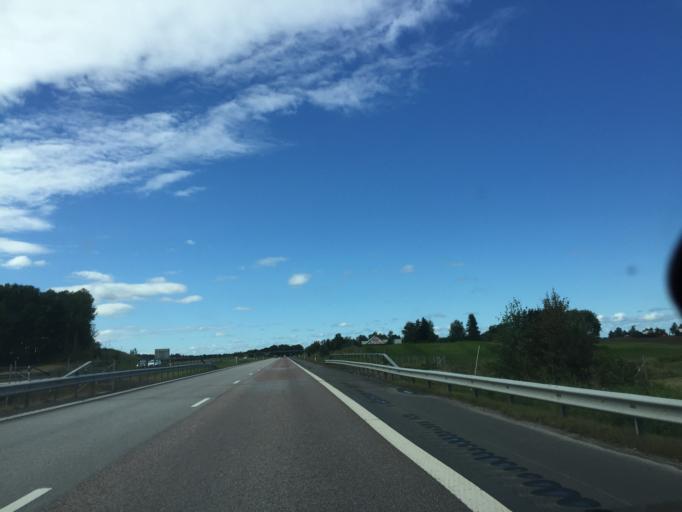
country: SE
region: OErebro
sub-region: Lindesbergs Kommun
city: Frovi
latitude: 59.3072
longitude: 15.3826
